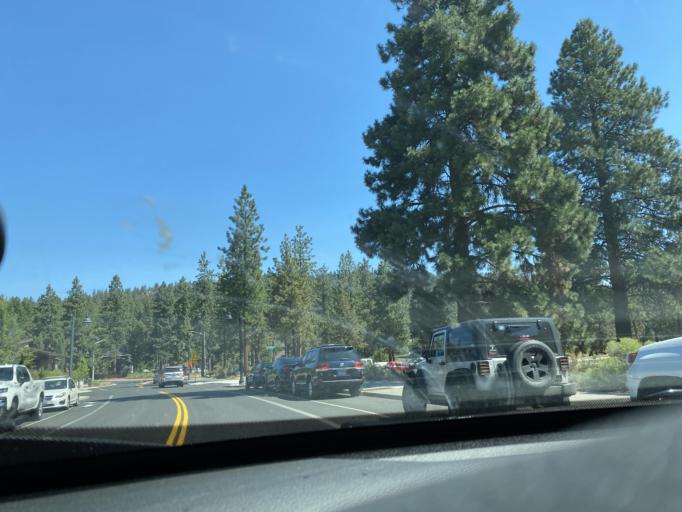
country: US
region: Oregon
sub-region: Deschutes County
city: Bend
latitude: 44.0628
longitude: -121.3455
